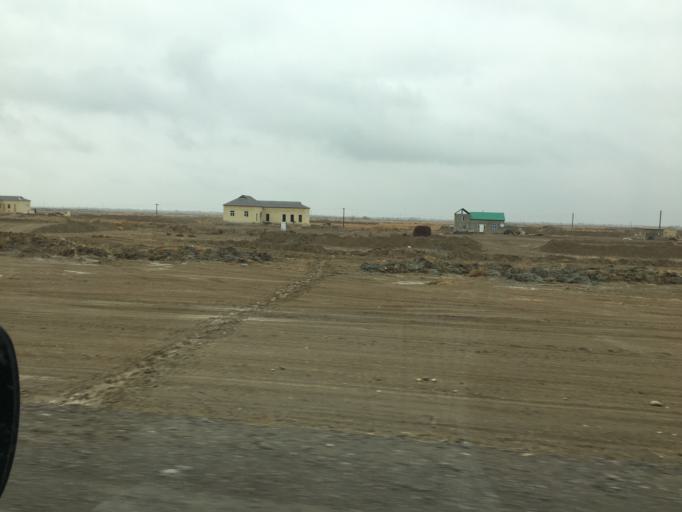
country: TM
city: Murgab
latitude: 37.4739
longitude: 62.0206
